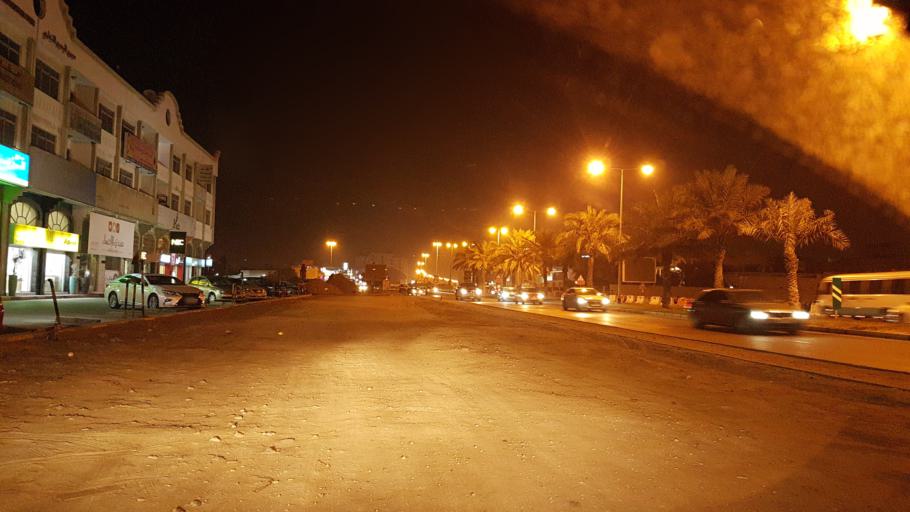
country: BH
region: Manama
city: Jidd Hafs
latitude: 26.2203
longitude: 50.4966
